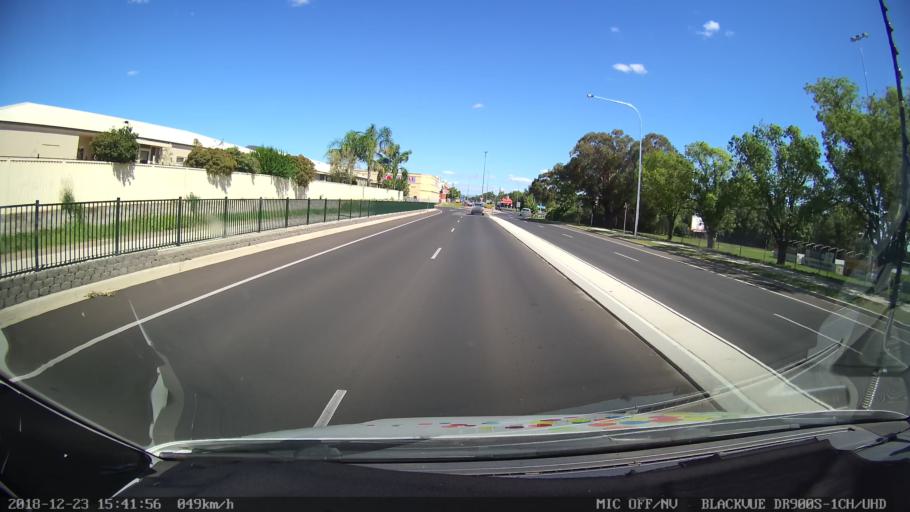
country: AU
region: New South Wales
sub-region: Tamworth Municipality
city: Tamworth
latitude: -31.0795
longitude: 150.9195
